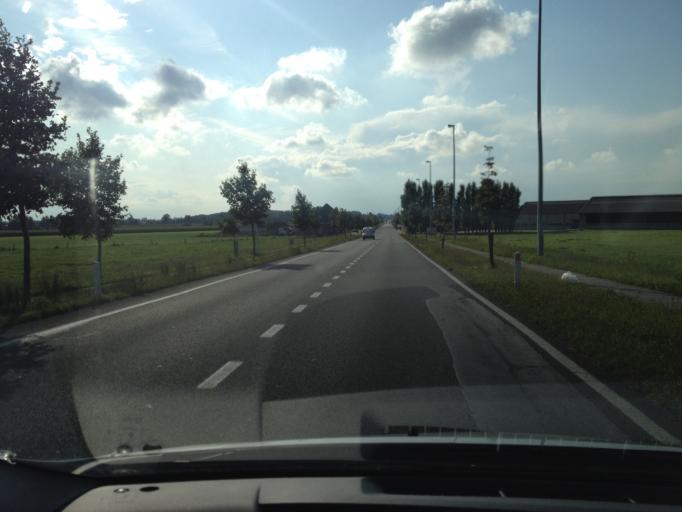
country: BE
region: Flanders
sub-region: Provincie West-Vlaanderen
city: Torhout
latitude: 51.1208
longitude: 3.0780
